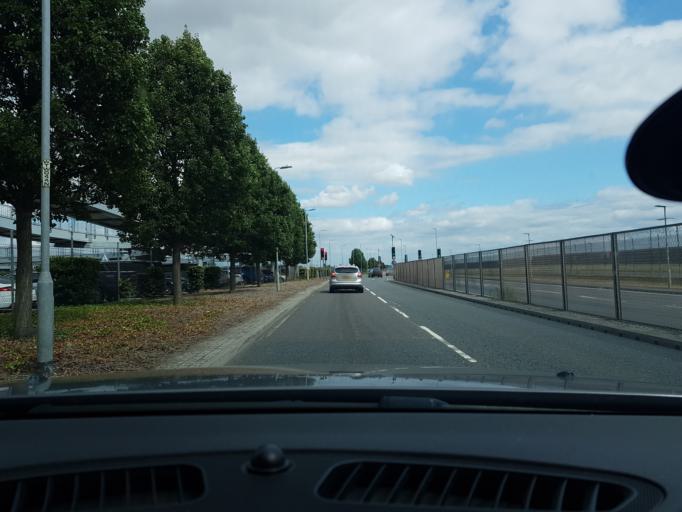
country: GB
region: England
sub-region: Buckinghamshire
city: Iver
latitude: 51.4793
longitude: -0.4880
